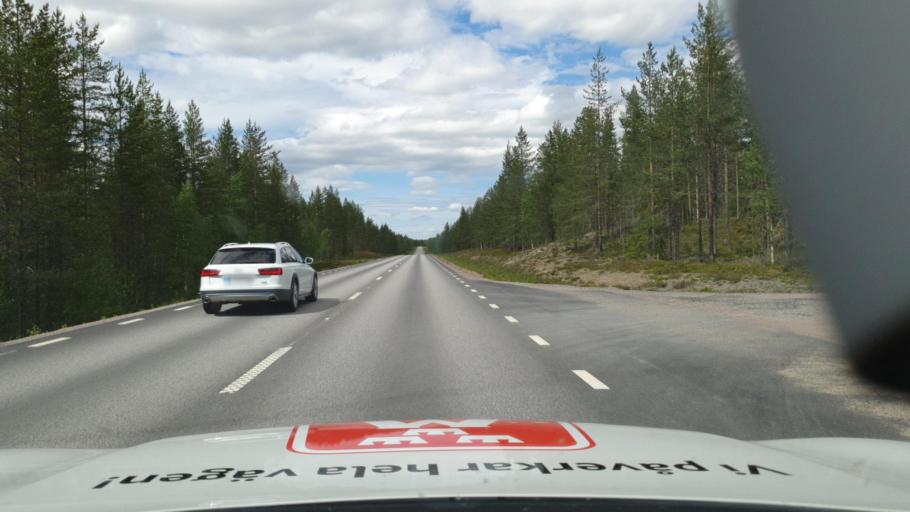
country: SE
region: Vaesterbotten
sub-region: Skelleftea Kommun
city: Langsele
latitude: 65.1330
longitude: 19.9175
